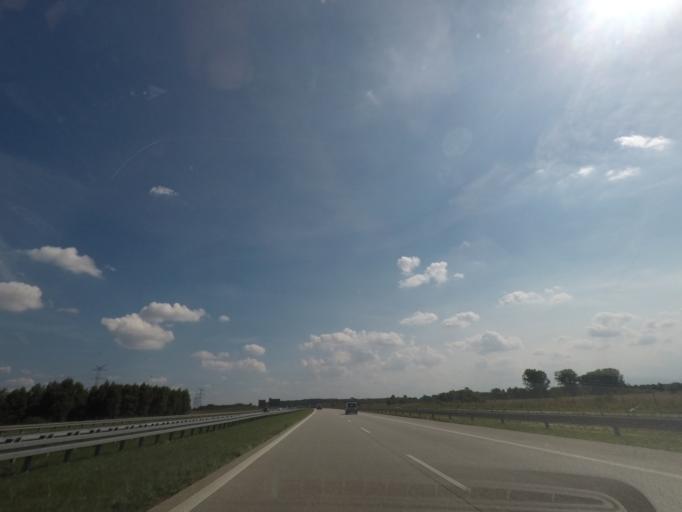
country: PL
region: Lodz Voivodeship
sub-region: Powiat lodzki wschodni
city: Tuszyn
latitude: 51.6196
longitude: 19.5689
